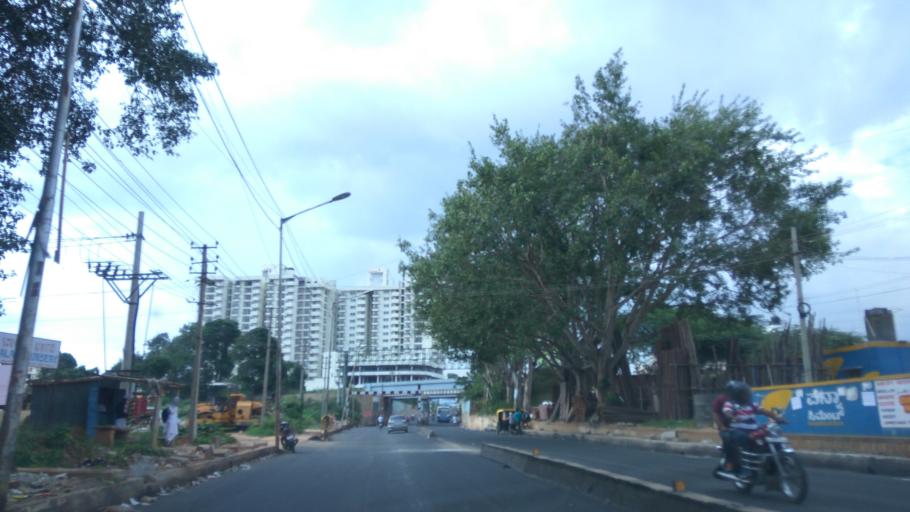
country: IN
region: Karnataka
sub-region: Bangalore Urban
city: Yelahanka
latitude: 13.0584
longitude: 77.6329
